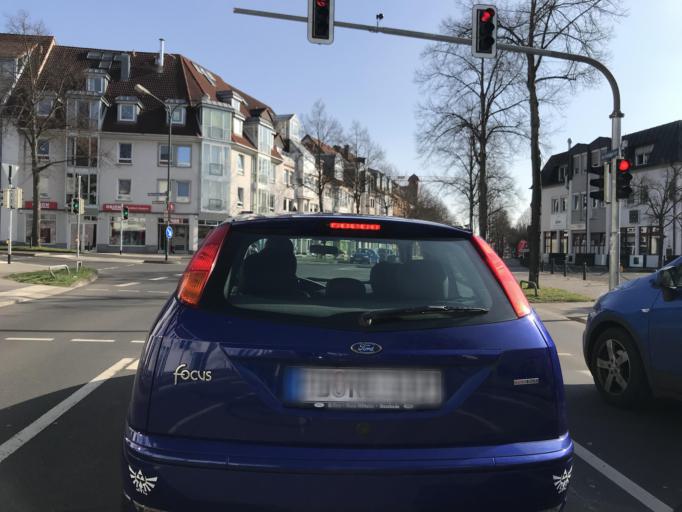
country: DE
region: Hesse
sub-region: Regierungsbezirk Kassel
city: Fulda
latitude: 50.5499
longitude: 9.6721
